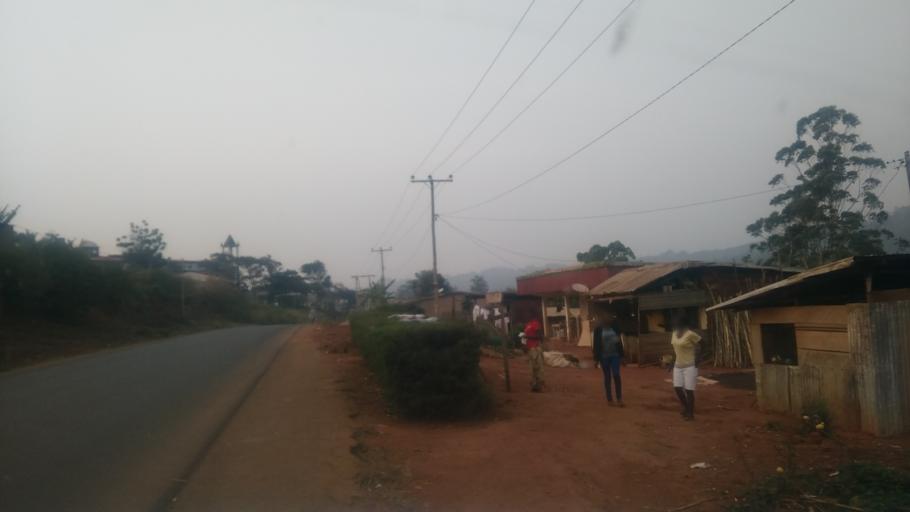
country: CM
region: West
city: Bana
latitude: 5.1437
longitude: 10.2756
